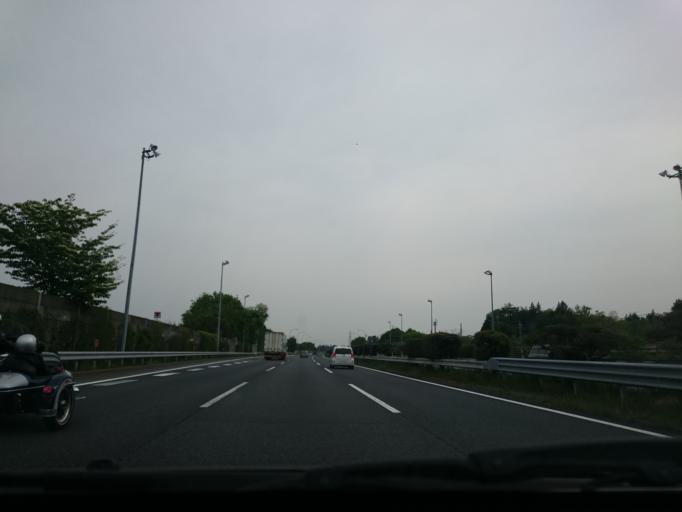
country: JP
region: Tochigi
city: Utsunomiya-shi
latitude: 36.6034
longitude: 139.8441
